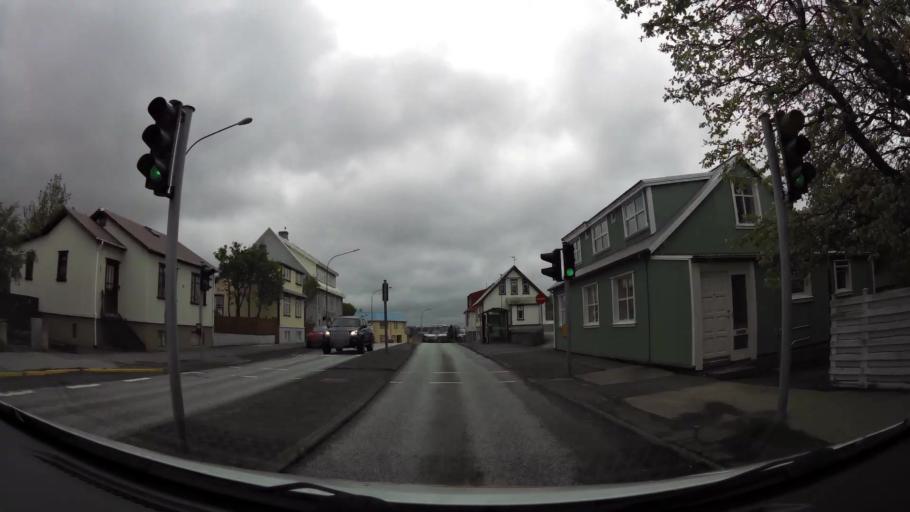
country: IS
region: Capital Region
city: Hafnarfjoerdur
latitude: 64.0720
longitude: -21.9547
